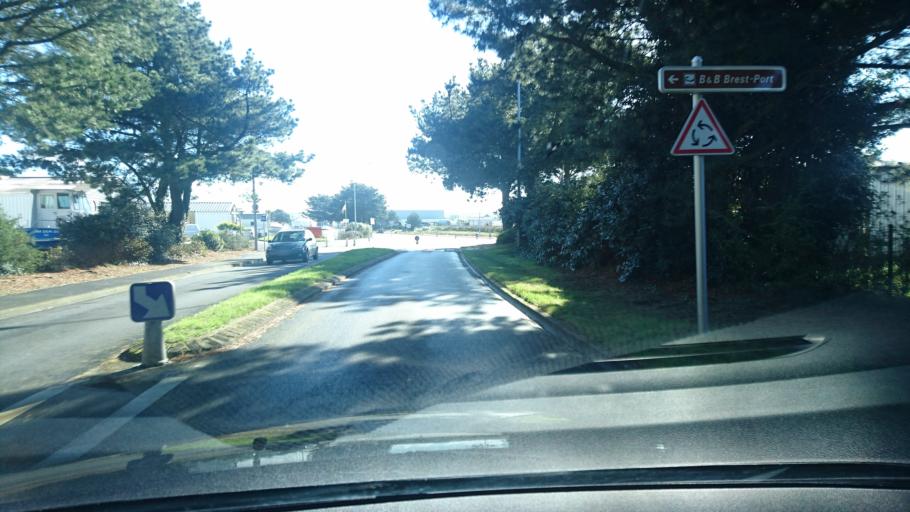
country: FR
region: Brittany
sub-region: Departement du Finistere
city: Brest
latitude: 48.3921
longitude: -4.4466
